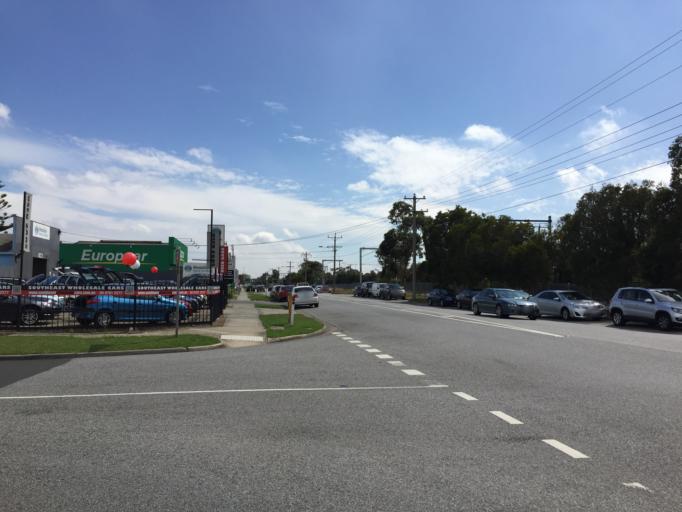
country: AU
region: Victoria
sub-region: Frankston
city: Frankston East
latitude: -38.1326
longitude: 145.1302
